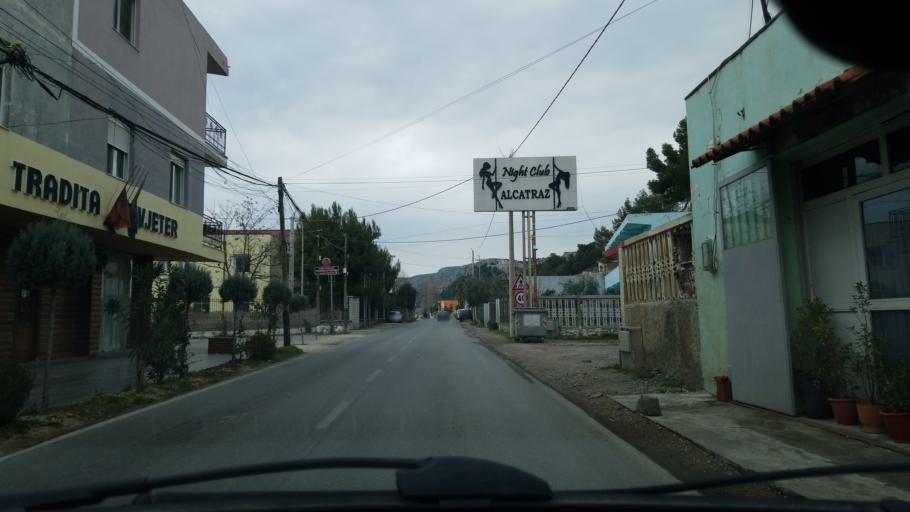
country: AL
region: Lezhe
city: Lezhe
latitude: 41.7792
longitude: 19.6328
